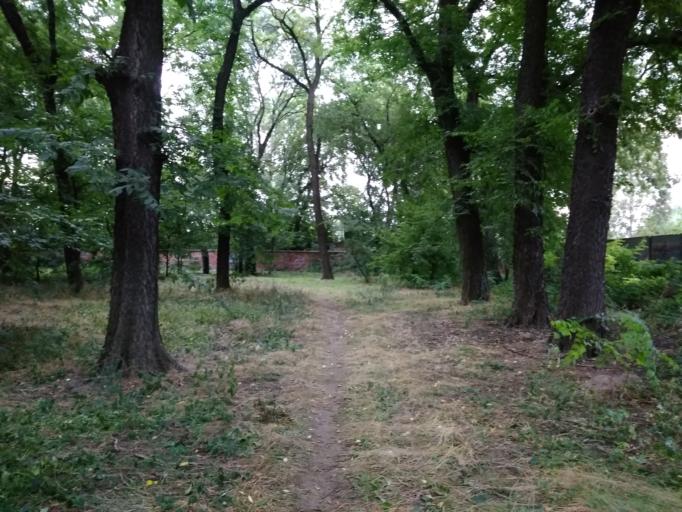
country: HU
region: Bekes
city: Oroshaza
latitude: 46.5683
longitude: 20.6649
